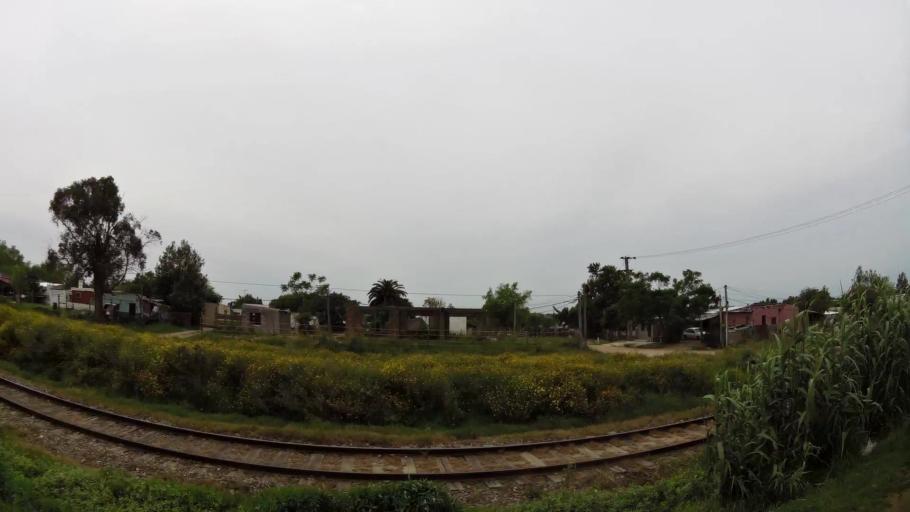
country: UY
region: Canelones
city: La Paz
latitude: -34.7491
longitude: -56.2219
